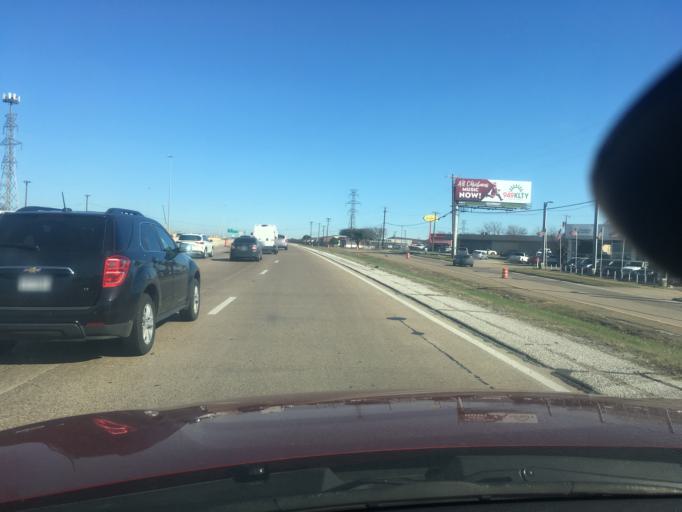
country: US
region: Texas
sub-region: Dallas County
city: Cockrell Hill
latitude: 32.6998
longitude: -96.8372
